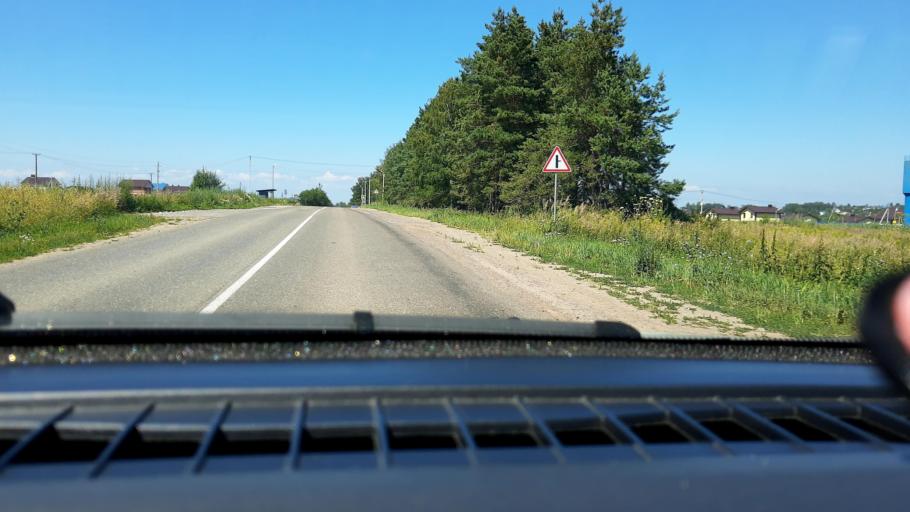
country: RU
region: Nizjnij Novgorod
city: Burevestnik
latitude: 56.1615
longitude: 43.7740
